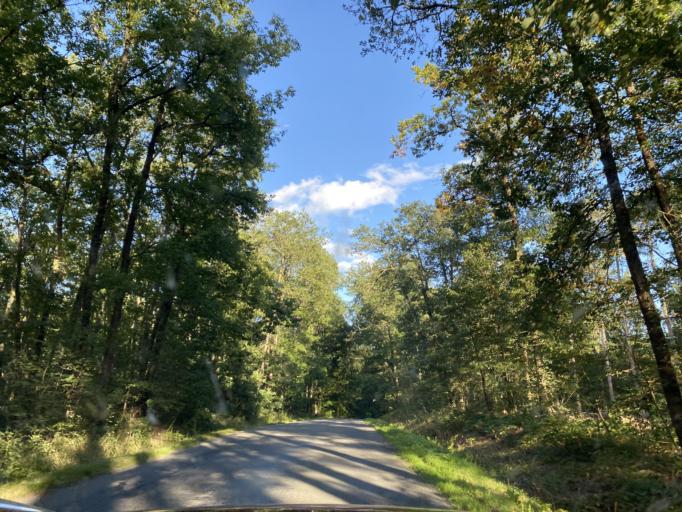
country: FR
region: Auvergne
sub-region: Departement de l'Allier
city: Brugheas
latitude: 46.0629
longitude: 3.3006
